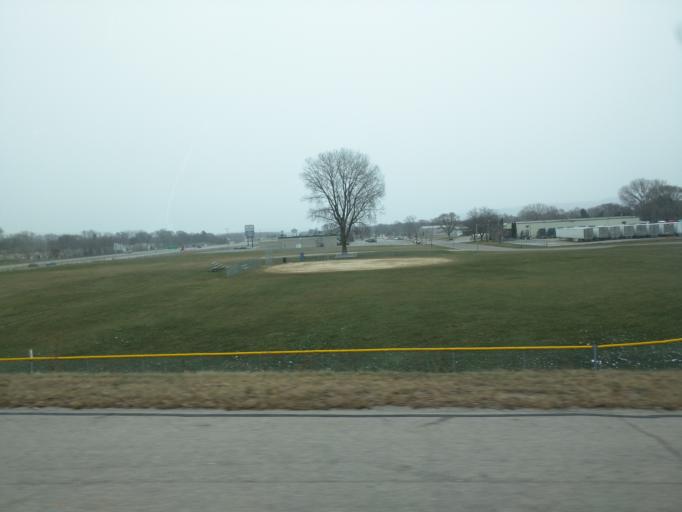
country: US
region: Wisconsin
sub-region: La Crosse County
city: French Island
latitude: 43.8592
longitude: -91.2697
